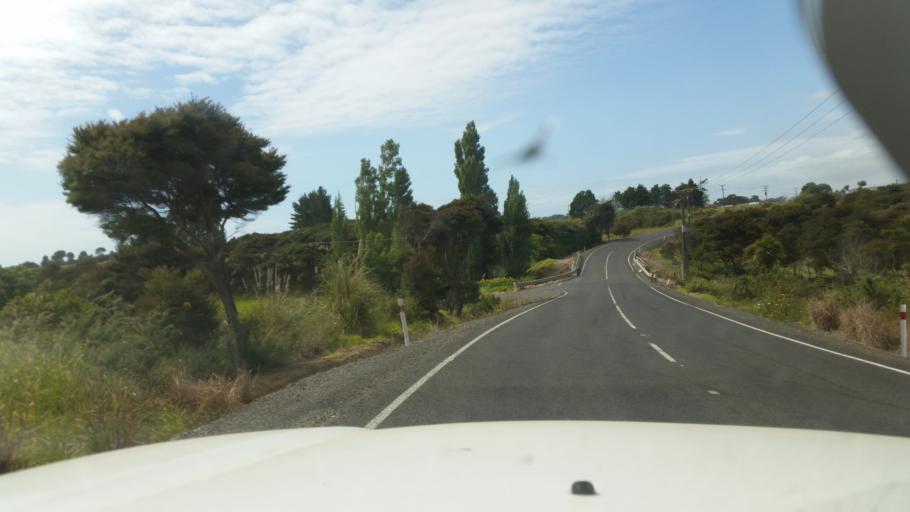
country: NZ
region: Northland
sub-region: Far North District
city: Ahipara
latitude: -35.1831
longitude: 173.1682
